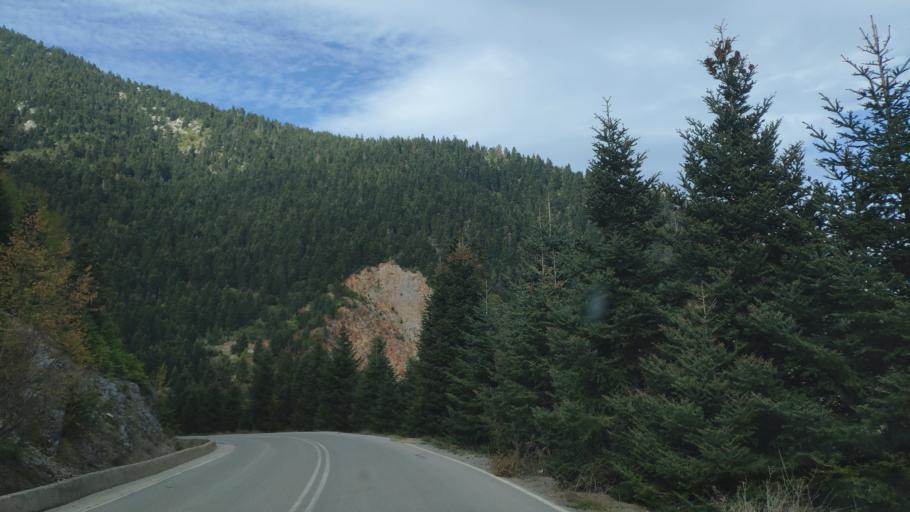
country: GR
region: Central Greece
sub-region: Nomos Fokidos
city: Amfissa
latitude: 38.6629
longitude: 22.3793
